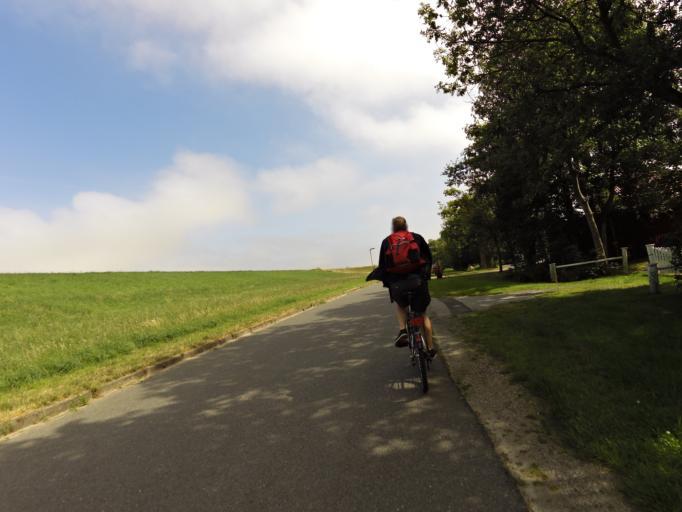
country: DE
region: Lower Saxony
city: Nordholz
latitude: 53.7955
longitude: 8.5605
